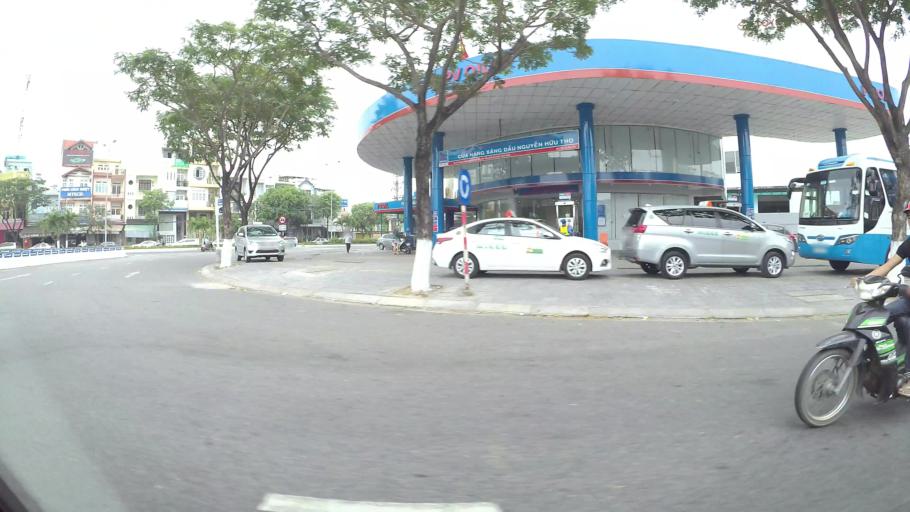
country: VN
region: Da Nang
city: Da Nang
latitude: 16.0499
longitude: 108.2095
